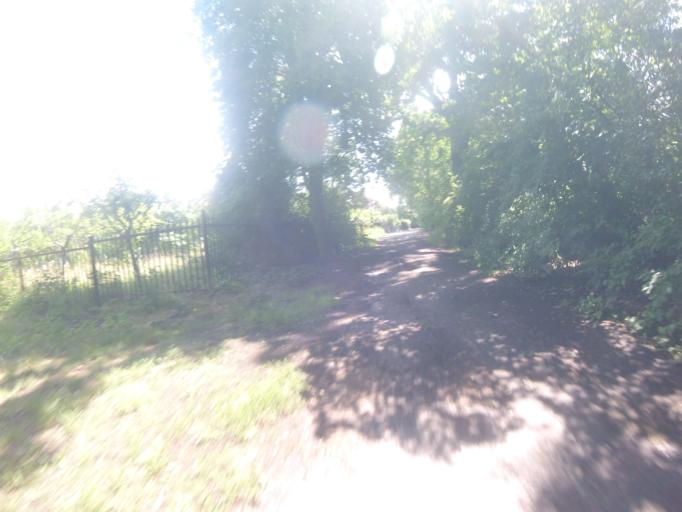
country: DE
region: Brandenburg
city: Konigs Wusterhausen
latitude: 52.2870
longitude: 13.6386
